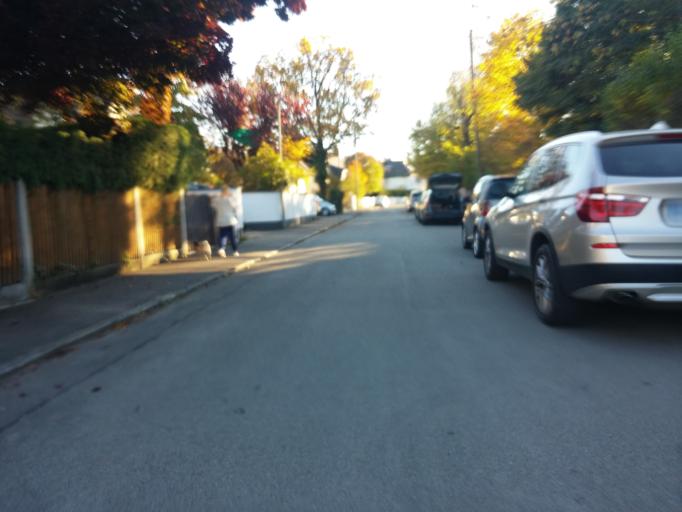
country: DE
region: Bavaria
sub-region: Upper Bavaria
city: Haar
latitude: 48.1112
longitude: 11.7051
